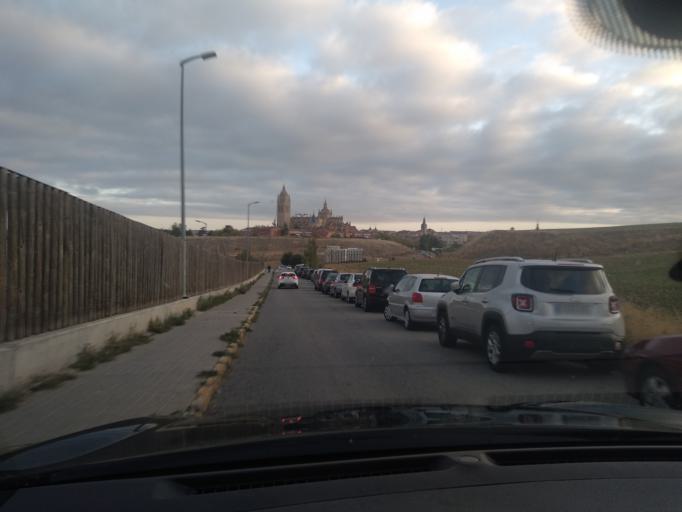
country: ES
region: Castille and Leon
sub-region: Provincia de Segovia
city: Segovia
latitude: 40.9429
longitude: -4.1275
